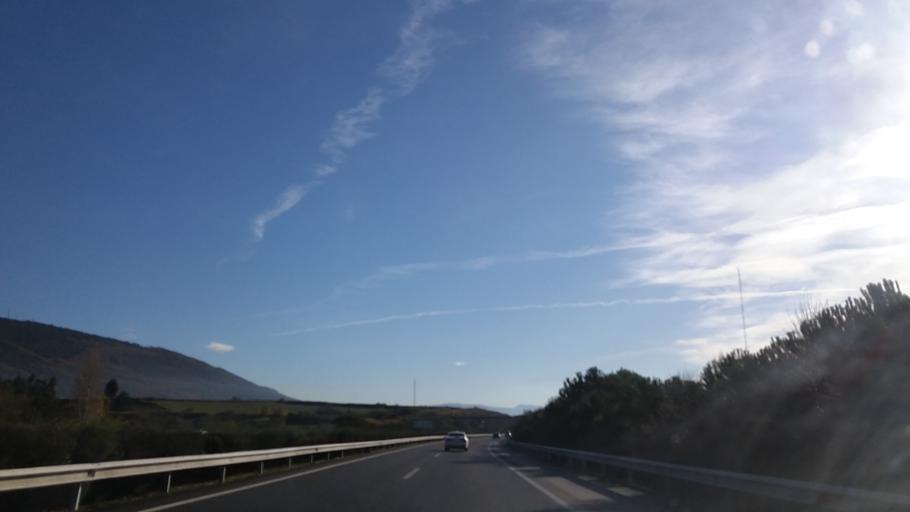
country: ES
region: Navarre
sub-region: Provincia de Navarra
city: Berriobeiti
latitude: 42.8487
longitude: -1.7034
